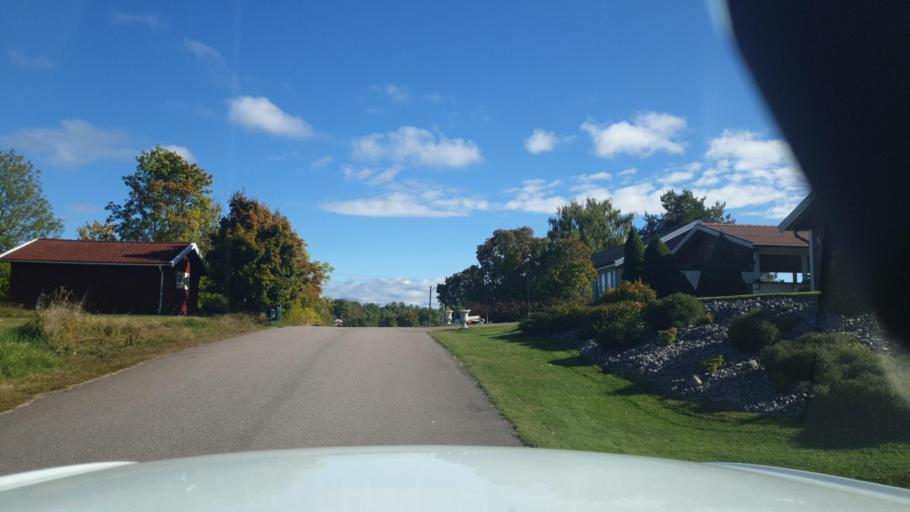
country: SE
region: Vaermland
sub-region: Karlstads Kommun
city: Edsvalla
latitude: 59.5584
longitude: 13.0524
